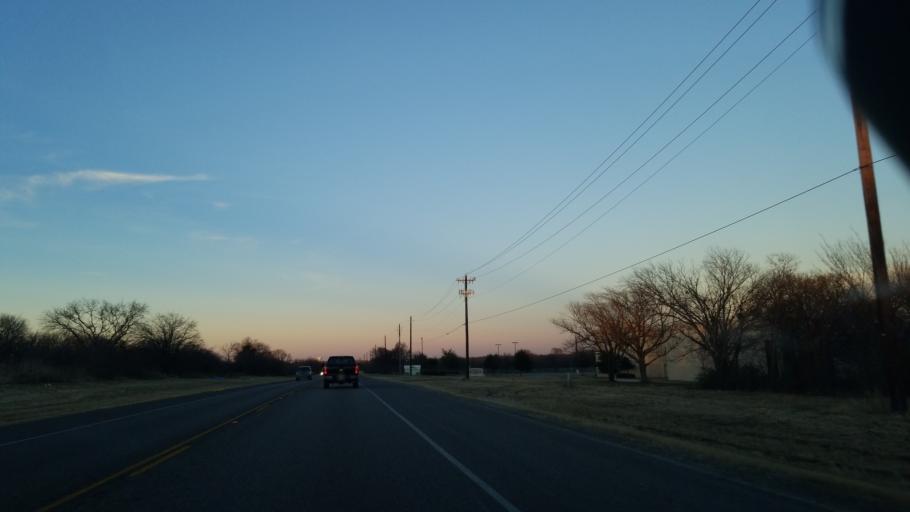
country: US
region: Texas
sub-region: Denton County
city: Argyle
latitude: 33.1390
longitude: -97.1747
